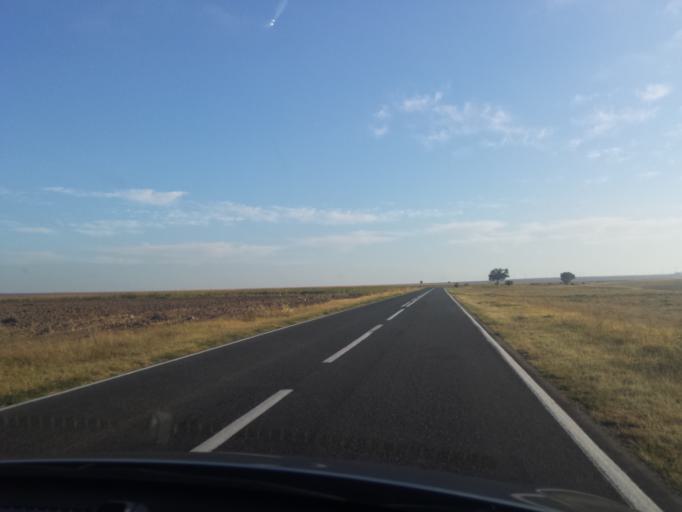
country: RO
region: Constanta
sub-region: Comuna Saraiu
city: Saraiu
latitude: 44.7353
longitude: 28.1709
